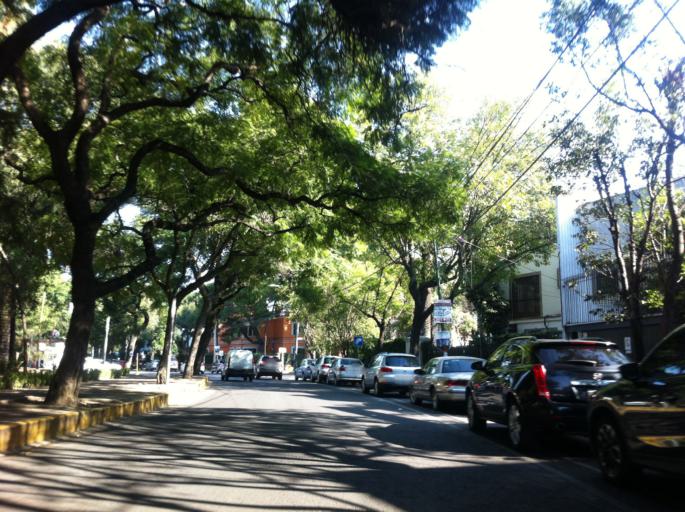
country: MX
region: Mexico City
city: Miguel Hidalgo
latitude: 19.4337
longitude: -99.1973
